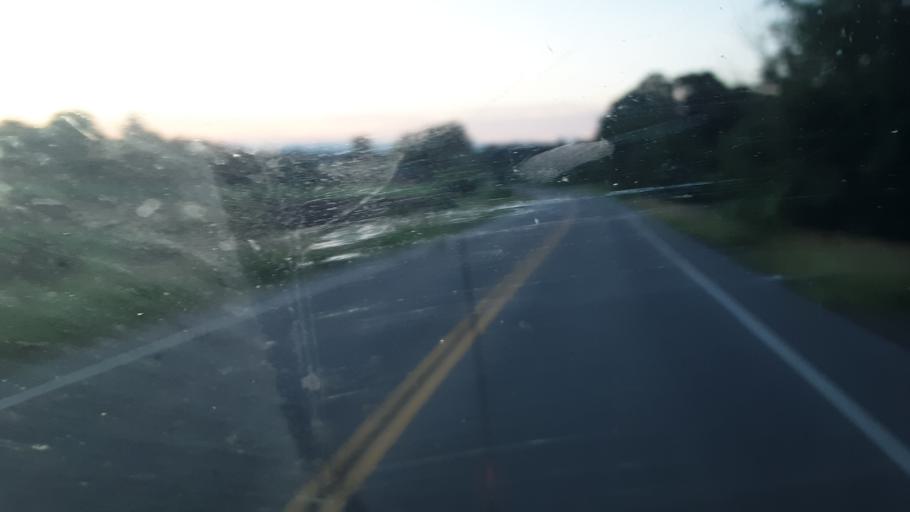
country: US
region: New York
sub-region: Schenectady County
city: East Glenville
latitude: 42.9748
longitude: -73.9883
